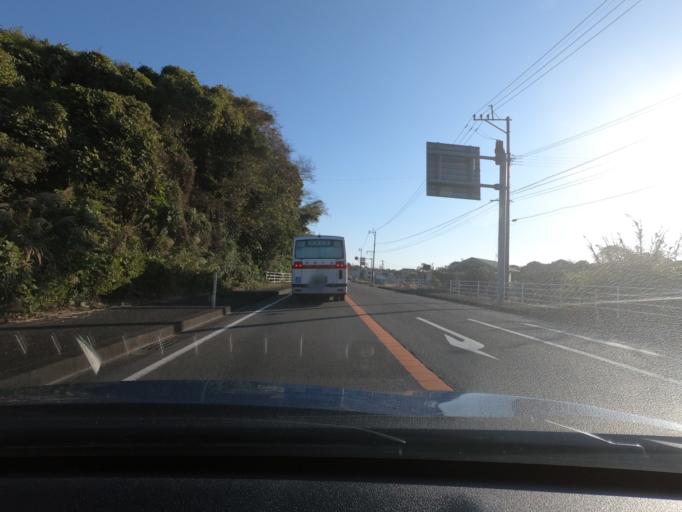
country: JP
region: Kagoshima
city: Akune
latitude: 31.9836
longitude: 130.2038
